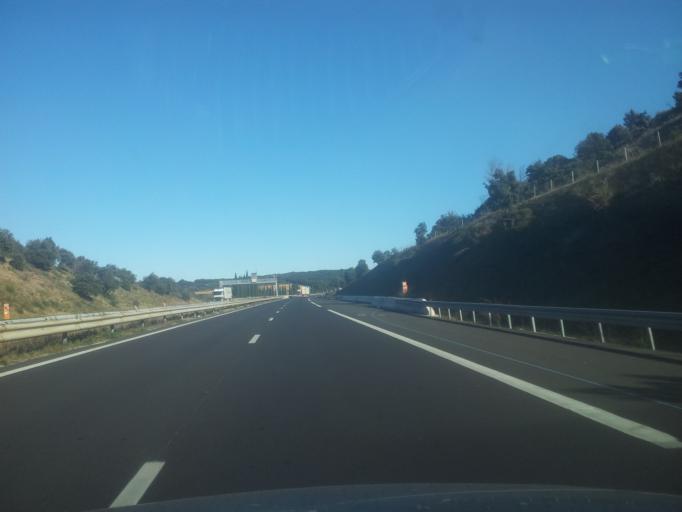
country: FR
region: Languedoc-Roussillon
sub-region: Departement du Gard
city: Tavel
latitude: 44.0126
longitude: 4.7178
